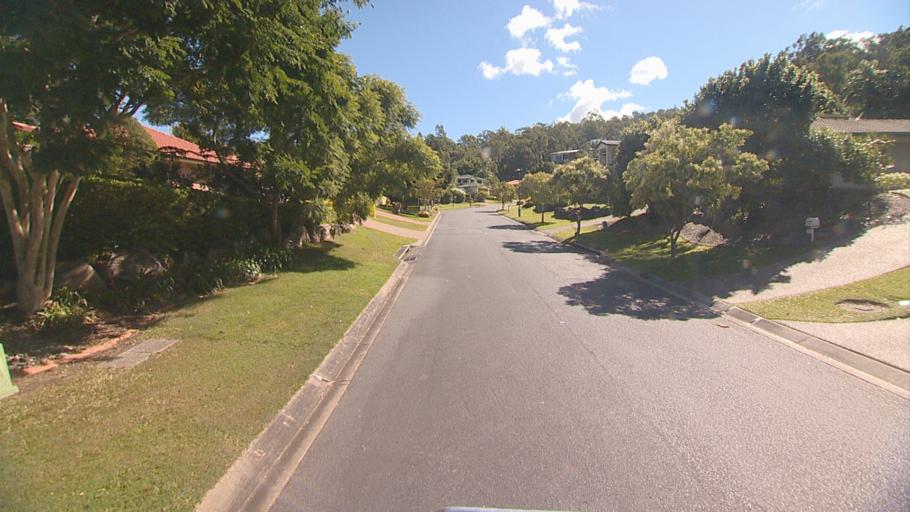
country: AU
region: Queensland
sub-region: Logan
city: Slacks Creek
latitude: -27.6512
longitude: 153.1911
